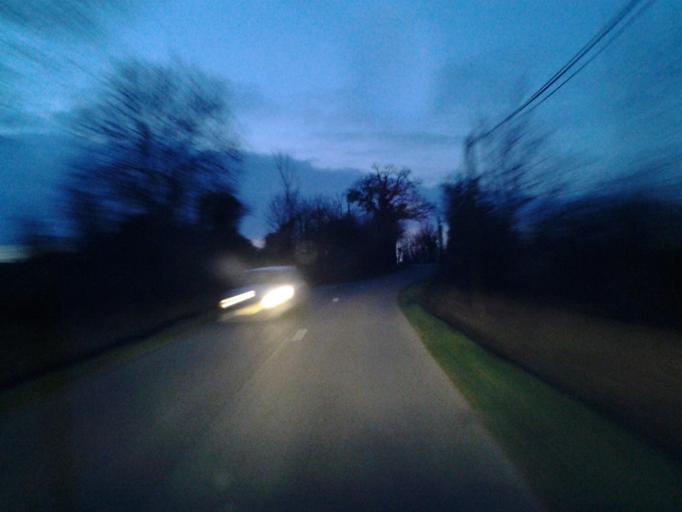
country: FR
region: Pays de la Loire
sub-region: Departement de la Vendee
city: Saint-Florent-des-Bois
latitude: 46.5715
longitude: -1.3395
